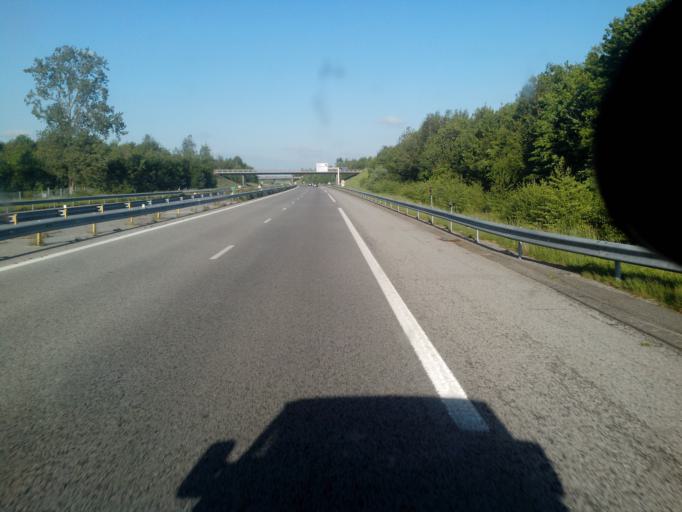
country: FR
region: Haute-Normandie
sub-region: Departement de la Seine-Maritime
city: Fauville-en-Caux
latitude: 49.6298
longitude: 0.6362
